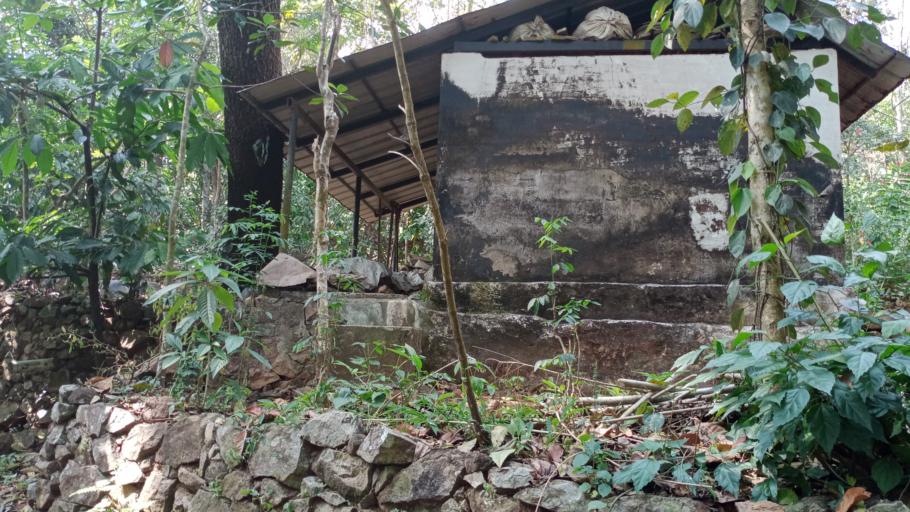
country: IN
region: Kerala
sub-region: Pattanamtitta
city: Pathanamthitta
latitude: 9.4278
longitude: 76.9137
